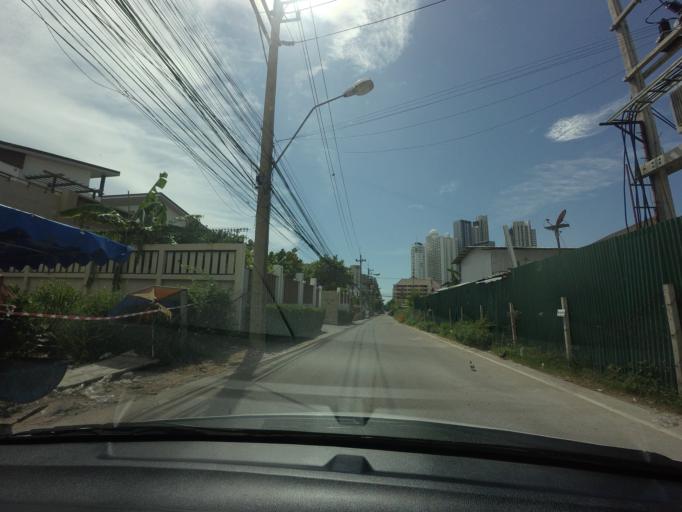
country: TH
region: Chon Buri
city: Phatthaya
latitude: 12.9581
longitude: 100.8901
